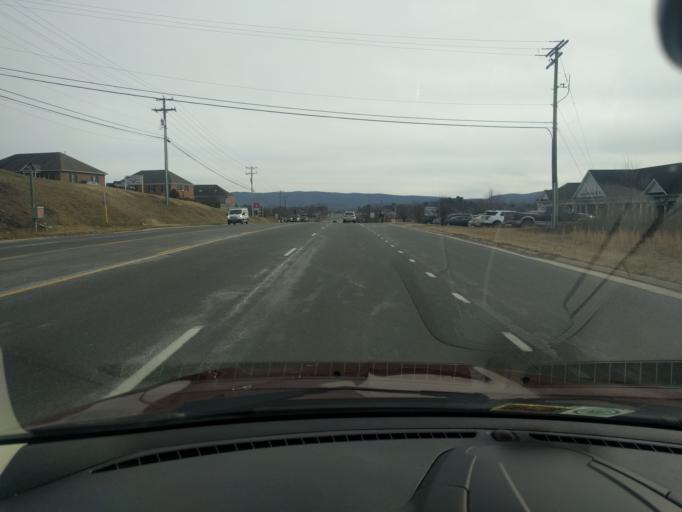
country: US
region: Virginia
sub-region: Augusta County
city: Fishersville
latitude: 38.0842
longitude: -78.9341
